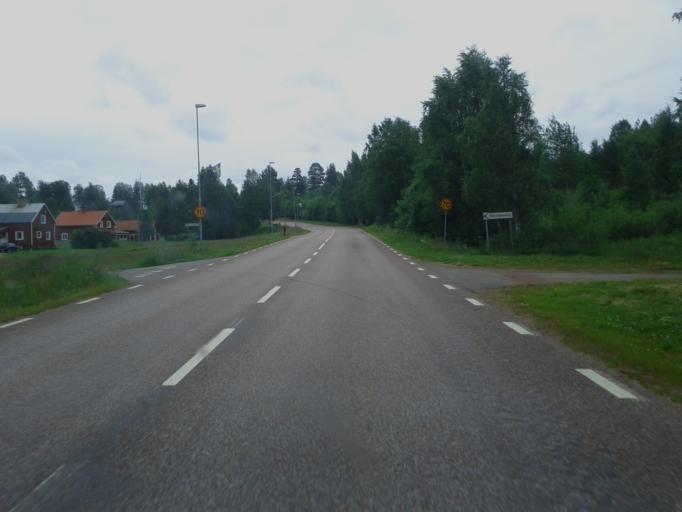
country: NO
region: Hedmark
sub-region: Trysil
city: Innbygda
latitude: 61.6907
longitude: 13.1520
